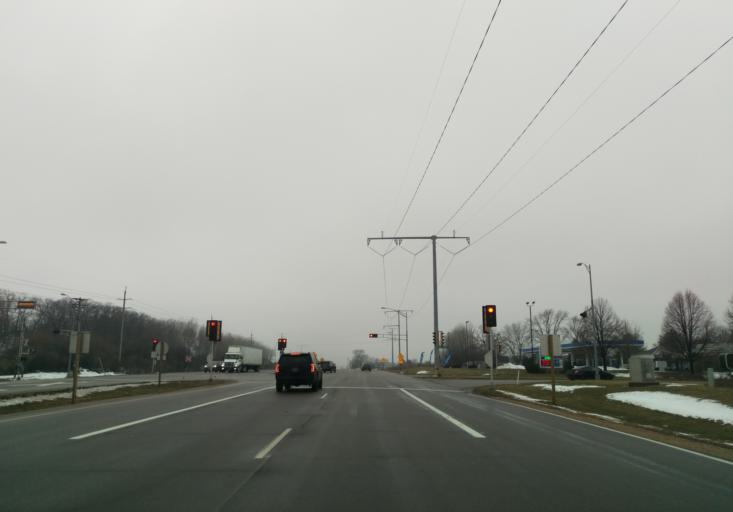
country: US
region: Wisconsin
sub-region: Dane County
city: Middleton
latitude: 43.0966
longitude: -89.5340
